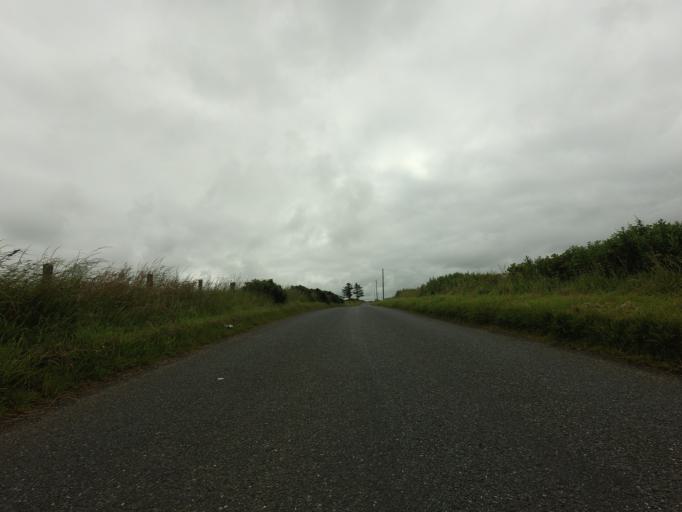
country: GB
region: Scotland
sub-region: Aberdeenshire
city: Rosehearty
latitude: 57.5420
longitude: -2.2092
